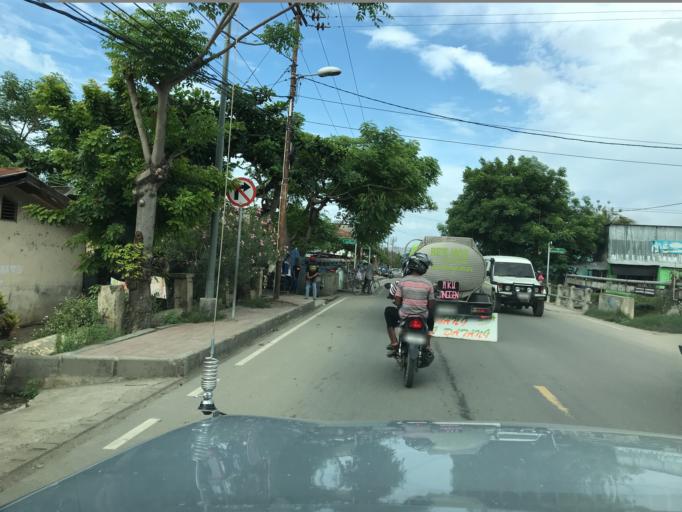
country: TL
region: Dili
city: Dili
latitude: -8.5593
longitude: 125.5645
